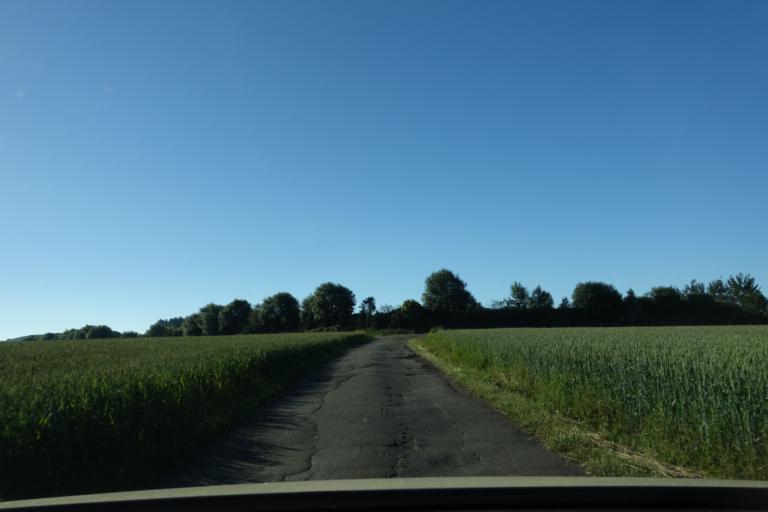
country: DE
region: Saxony
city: Eppendorf
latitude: 50.7788
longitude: 13.2385
